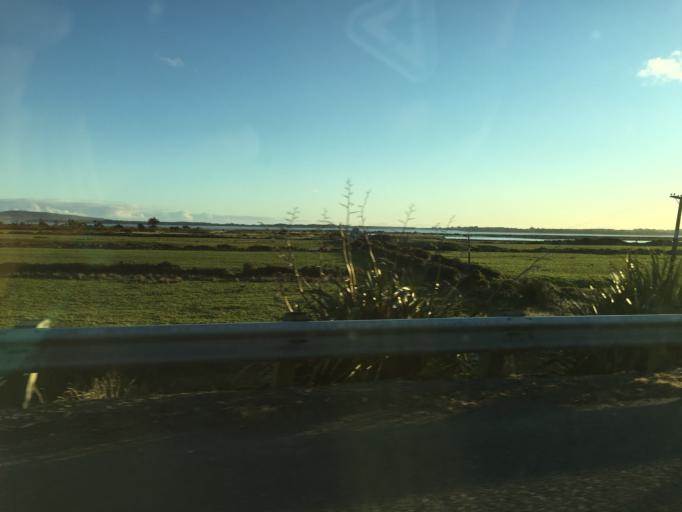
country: NZ
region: Southland
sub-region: Invercargill City
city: Invercargill
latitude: -46.4559
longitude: 168.3651
